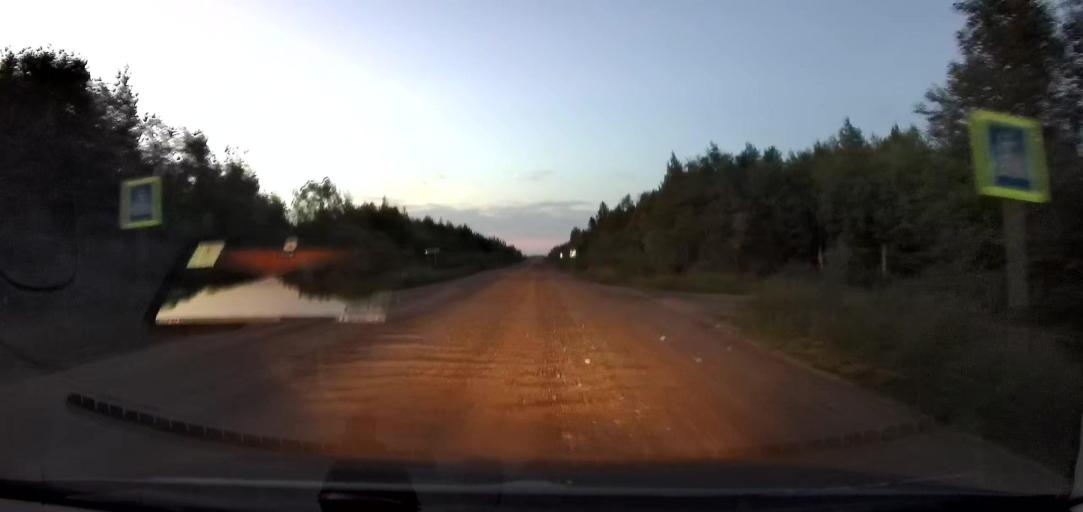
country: RU
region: Arkhangelskaya
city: Kholmogory
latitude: 64.3292
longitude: 41.4313
